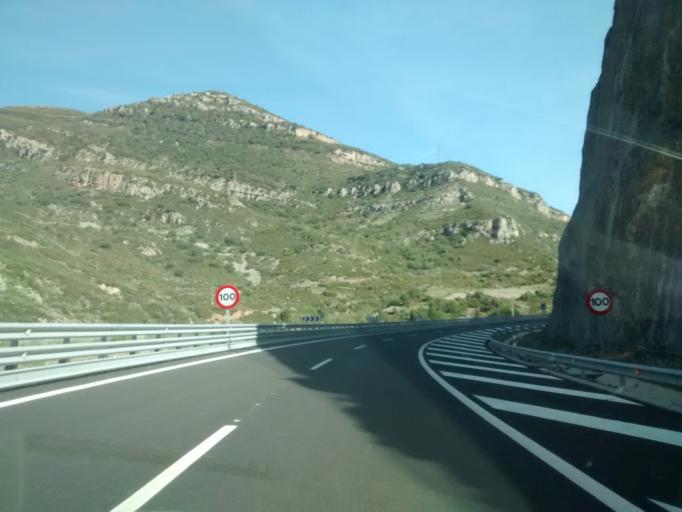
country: ES
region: Aragon
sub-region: Provincia de Huesca
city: Nueno
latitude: 42.2833
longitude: -0.4244
